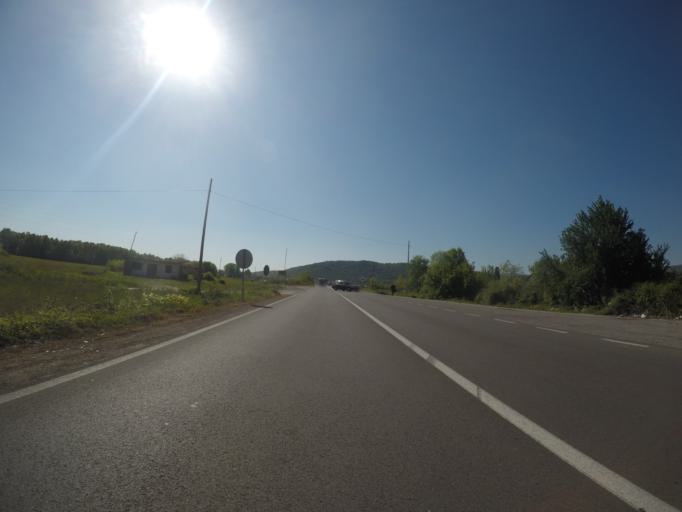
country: ME
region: Danilovgrad
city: Danilovgrad
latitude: 42.5171
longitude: 19.1234
